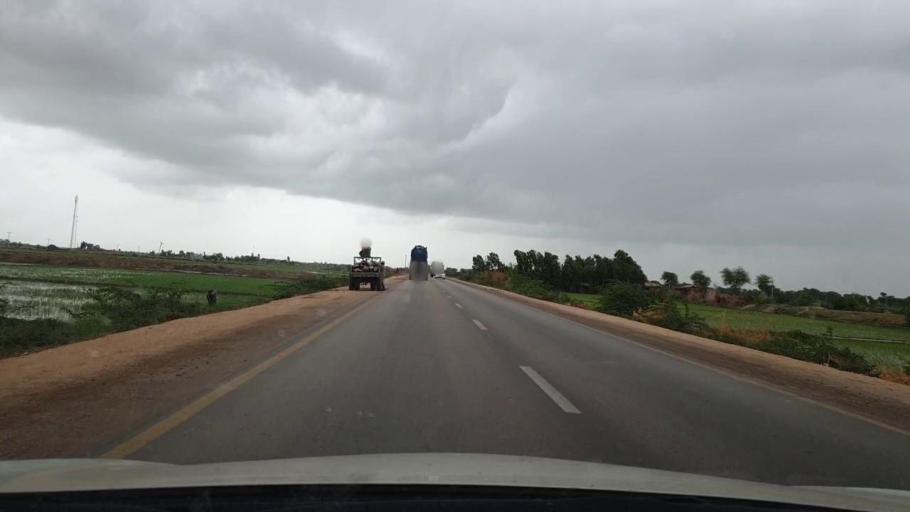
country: PK
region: Sindh
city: Kario
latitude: 24.6444
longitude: 68.4793
